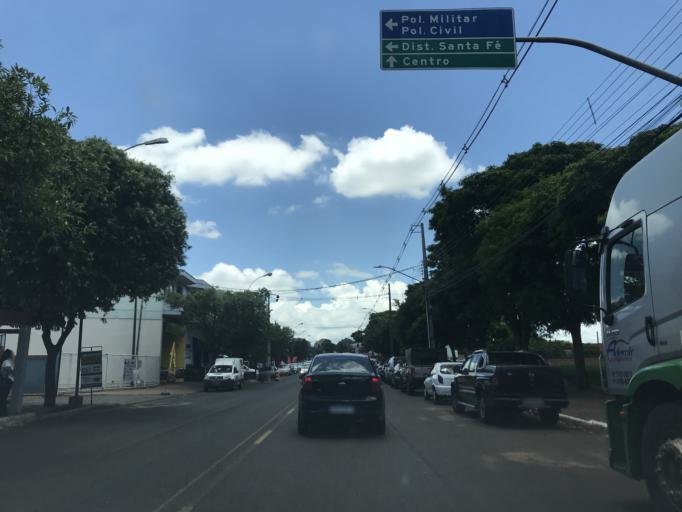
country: BR
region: Parana
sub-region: Marialva
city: Marialva
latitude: -23.4817
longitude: -51.8018
